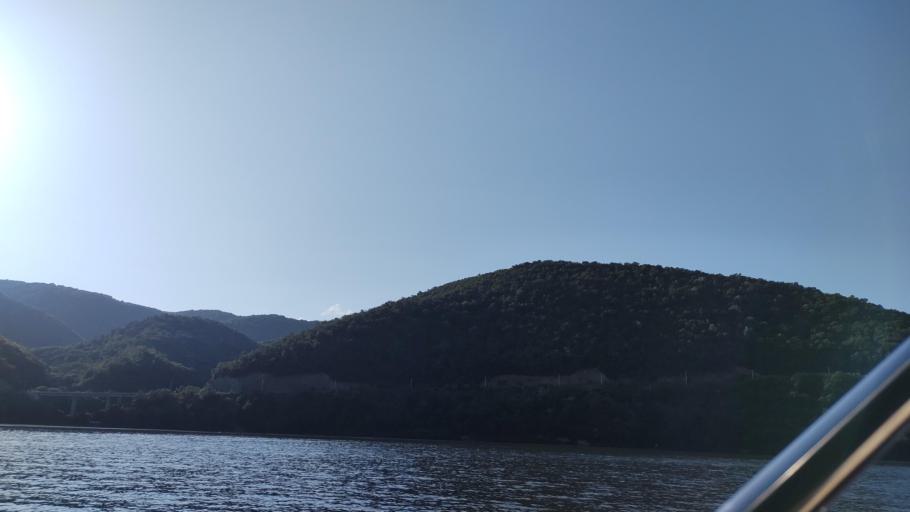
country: RO
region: Mehedinti
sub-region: Comuna Dubova
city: Dubova
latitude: 44.5847
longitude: 22.2531
